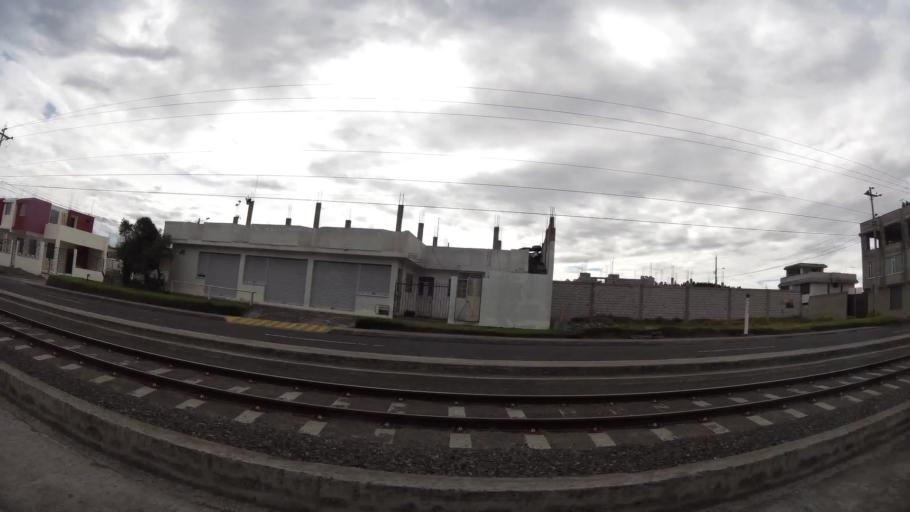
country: EC
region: Cotopaxi
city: Latacunga
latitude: -0.9493
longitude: -78.6164
